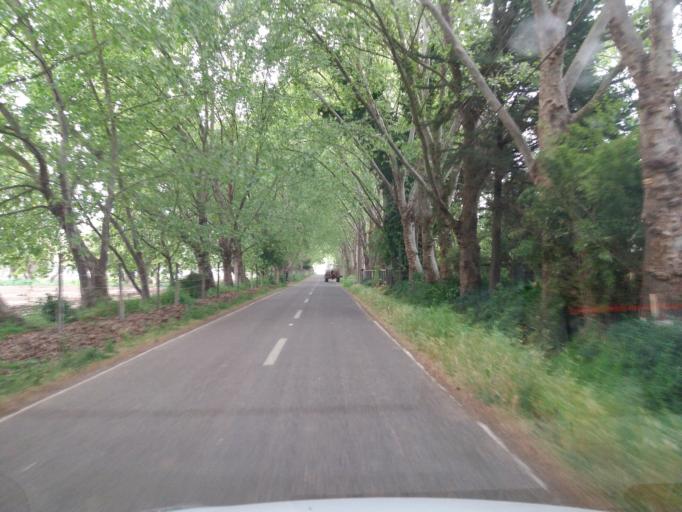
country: CL
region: Valparaiso
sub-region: Provincia de Quillota
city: Quillota
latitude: -32.8912
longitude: -71.3160
